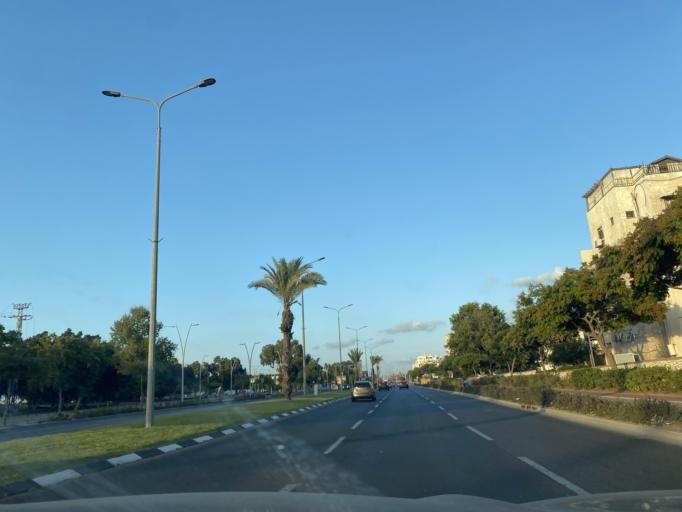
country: IL
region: Southern District
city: Ashdod
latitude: 31.8030
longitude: 34.6580
